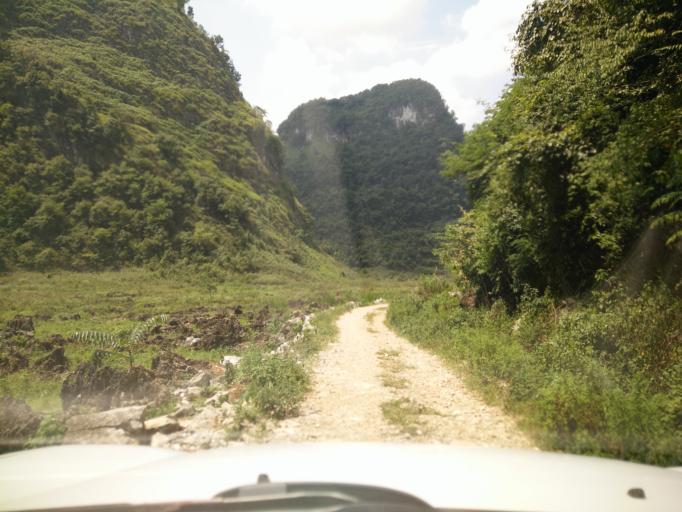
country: CN
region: Guangxi Zhuangzu Zizhiqu
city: Xinzhou
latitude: 25.0096
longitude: 105.7063
